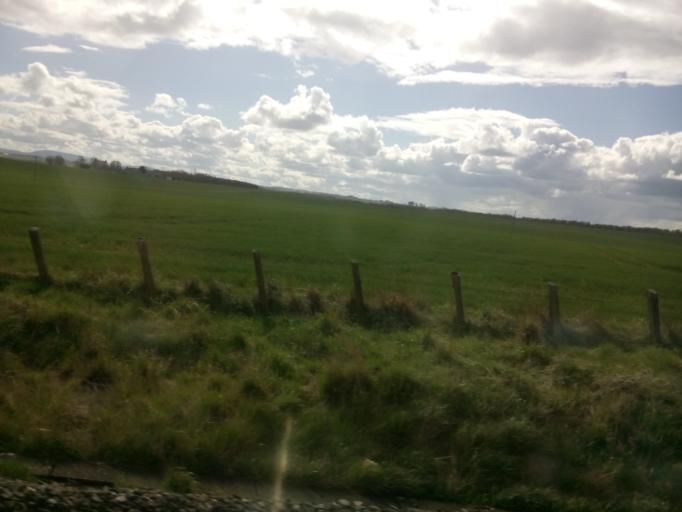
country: GB
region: England
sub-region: Northumberland
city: Ancroft
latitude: 55.7094
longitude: -1.9321
